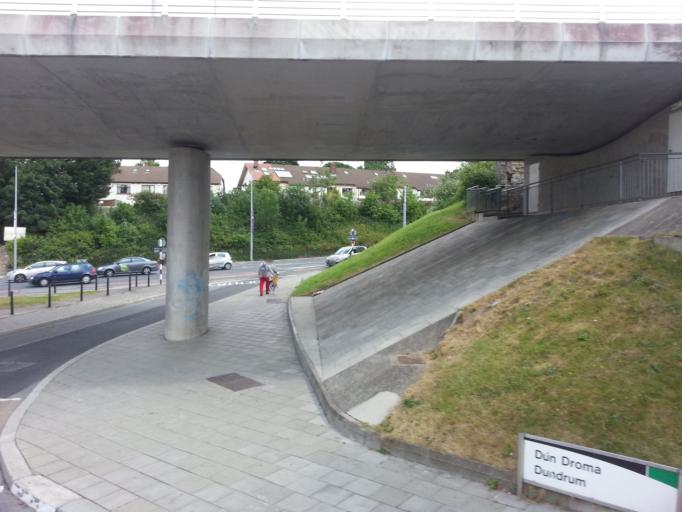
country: IE
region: Leinster
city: Dundrum
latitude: 53.2926
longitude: -6.2458
